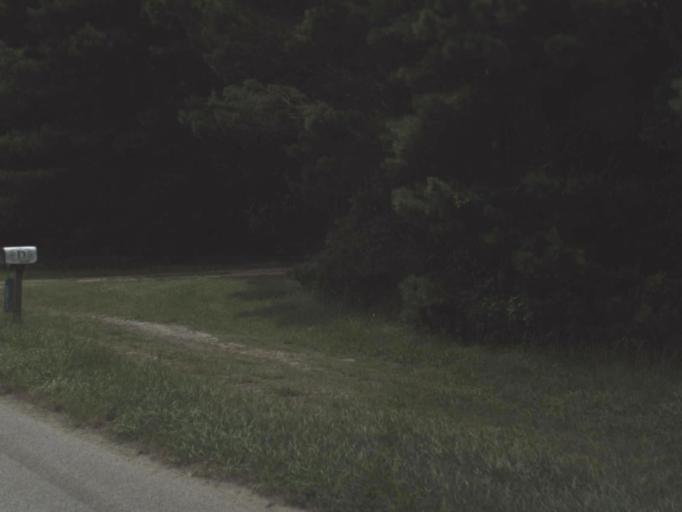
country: US
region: Florida
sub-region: Madison County
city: Madison
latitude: 30.4722
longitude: -83.2838
